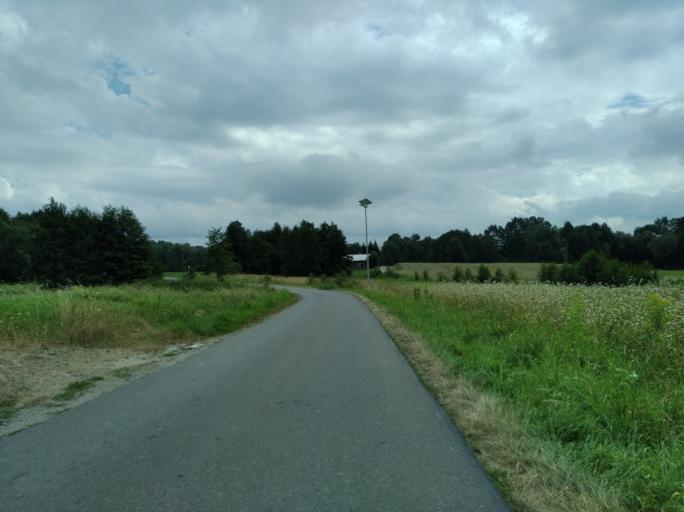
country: PL
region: Subcarpathian Voivodeship
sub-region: Powiat krosnienski
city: Odrzykon
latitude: 49.7403
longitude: 21.7600
